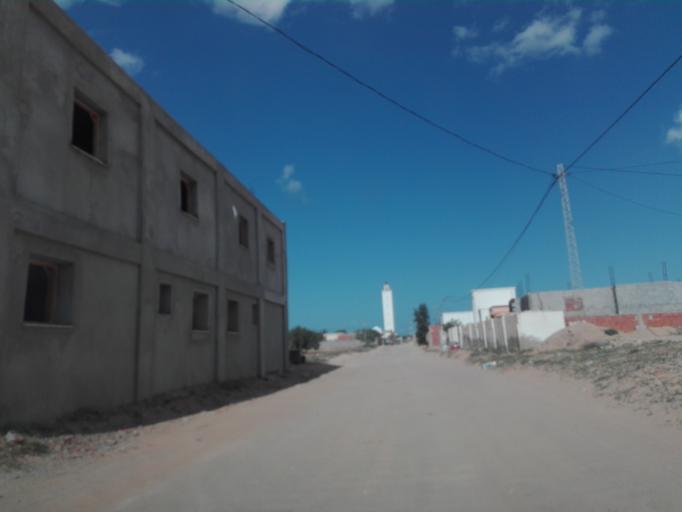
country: TN
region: Madanin
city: Bin Qirdan
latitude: 33.1582
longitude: 11.1944
